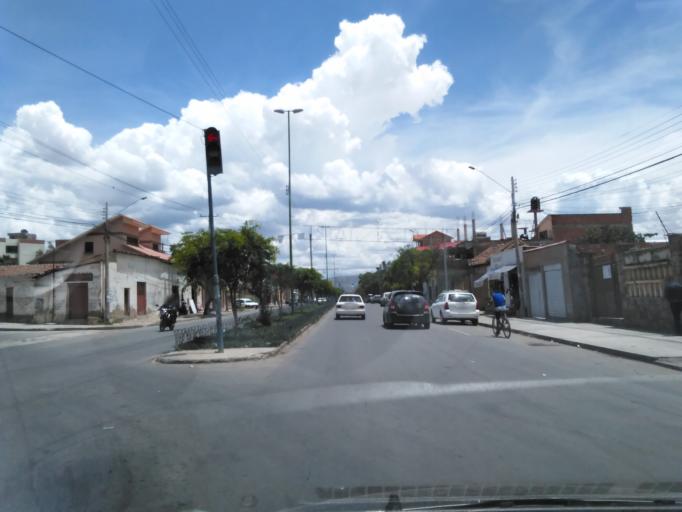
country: BO
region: Cochabamba
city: Cochabamba
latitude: -17.4122
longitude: -66.1649
